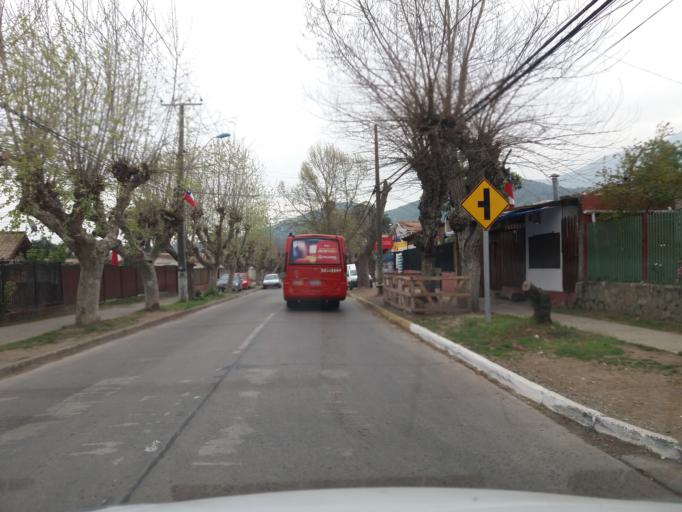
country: CL
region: Valparaiso
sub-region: Provincia de Quillota
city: Hacienda La Calera
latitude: -32.7967
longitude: -71.1471
